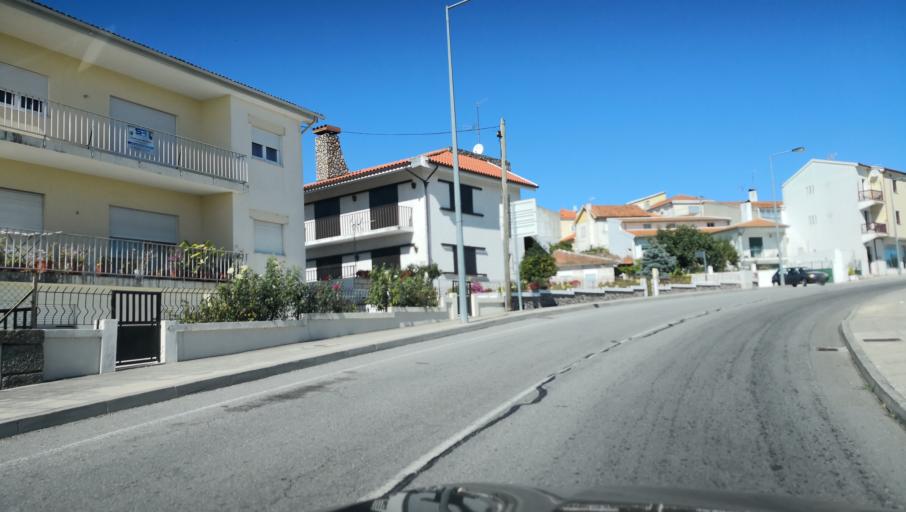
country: PT
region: Vila Real
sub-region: Valpacos
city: Valpacos
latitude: 41.6123
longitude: -7.3128
